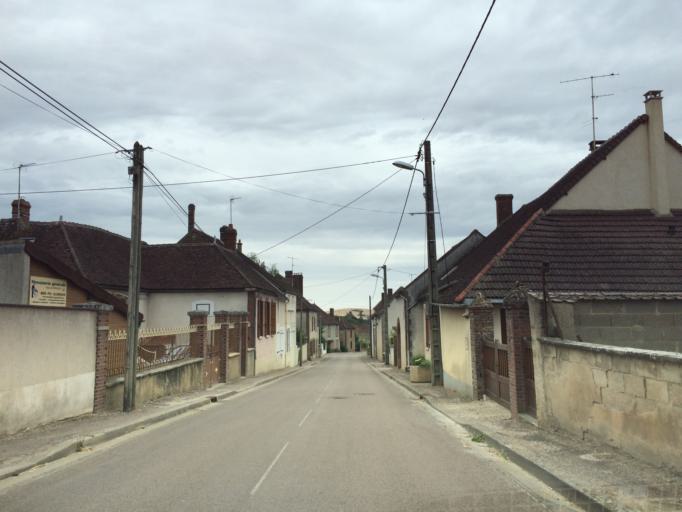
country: FR
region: Bourgogne
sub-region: Departement de l'Yonne
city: Aillant-sur-Tholon
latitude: 47.8725
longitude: 3.3416
